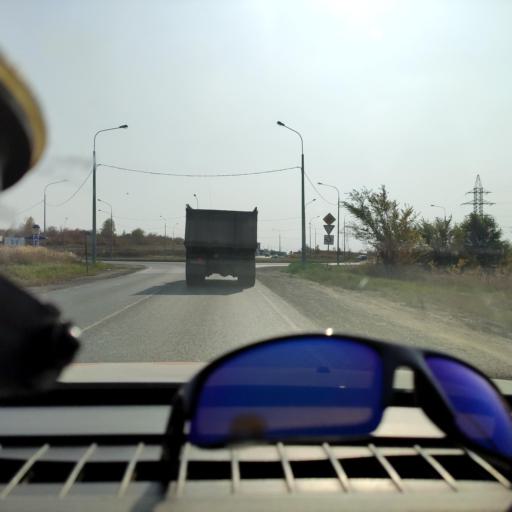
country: RU
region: Samara
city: Chapayevsk
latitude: 52.9983
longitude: 49.7680
